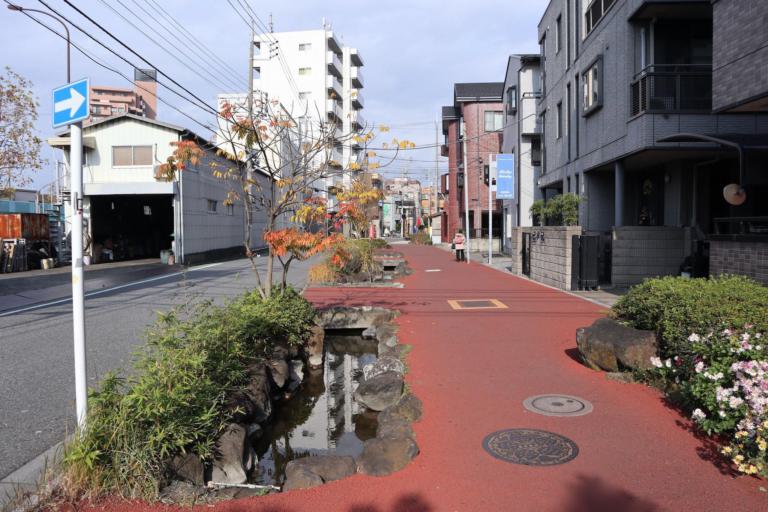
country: JP
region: Tokyo
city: Urayasu
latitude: 35.6887
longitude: 139.8834
